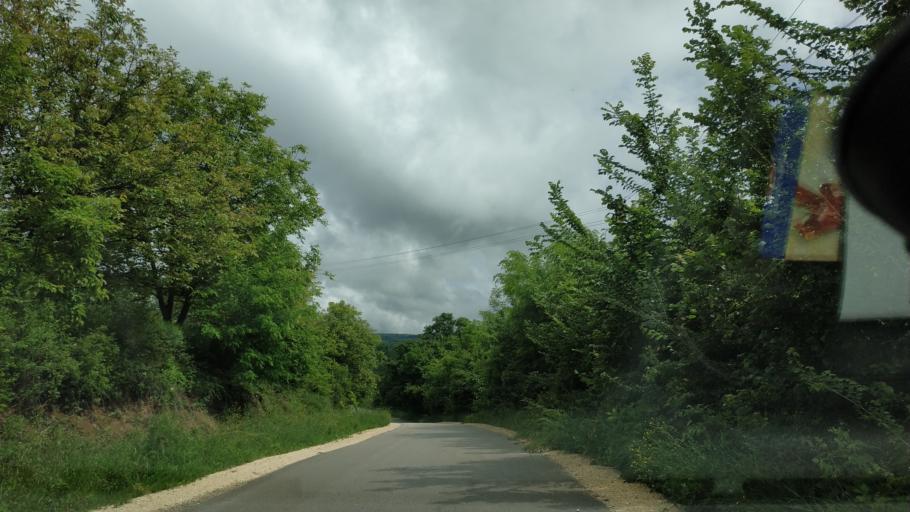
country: RS
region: Central Serbia
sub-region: Zajecarski Okrug
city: Soko Banja
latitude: 43.6531
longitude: 21.9030
